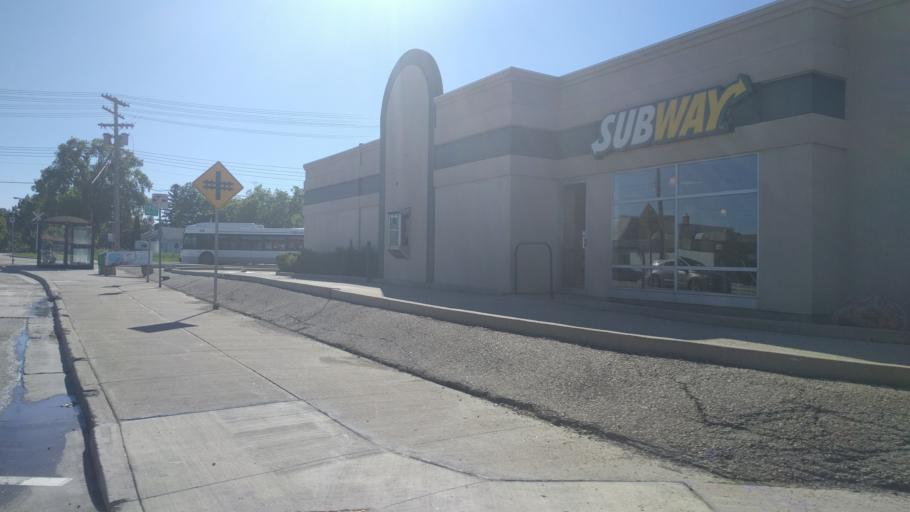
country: CA
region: Manitoba
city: Winnipeg
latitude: 49.8480
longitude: -97.1532
